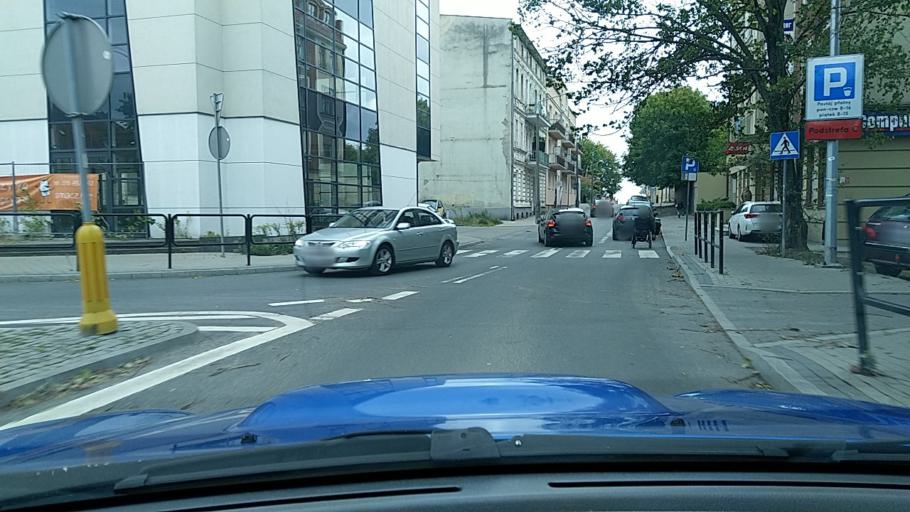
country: PL
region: Warmian-Masurian Voivodeship
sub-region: Powiat olsztynski
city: Olsztyn
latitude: 53.7817
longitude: 20.4789
